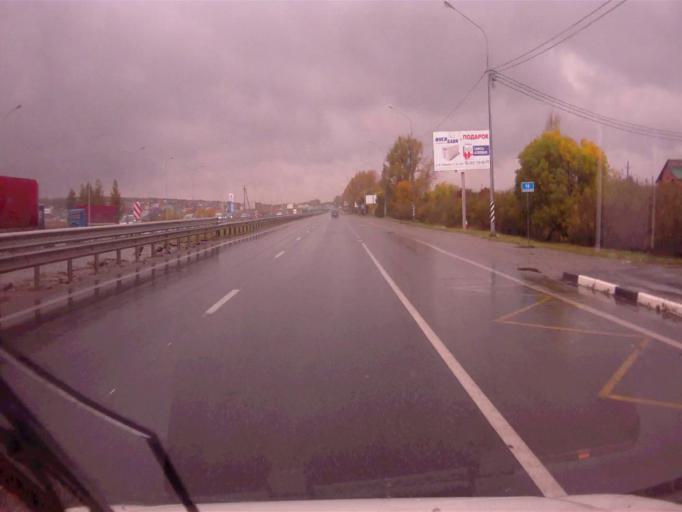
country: RU
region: Chelyabinsk
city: Dolgoderevenskoye
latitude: 55.2756
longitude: 61.3439
